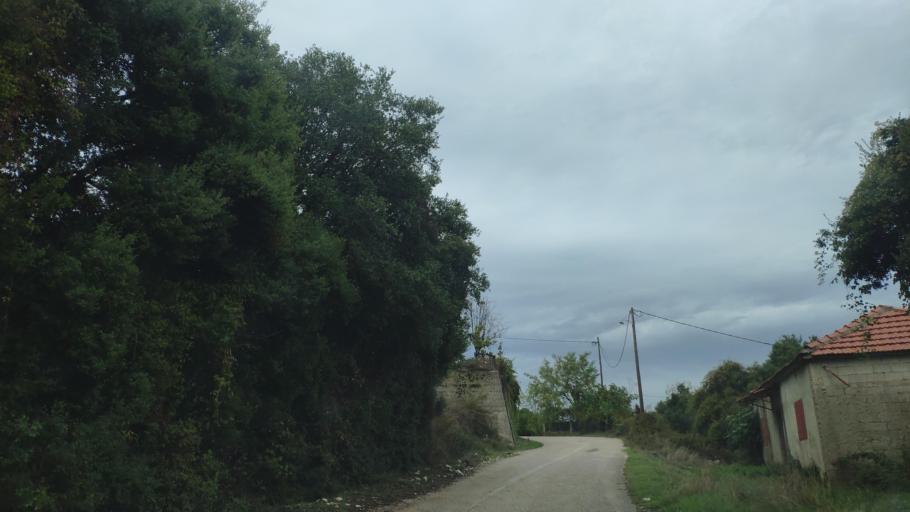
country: GR
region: Epirus
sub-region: Nomos Thesprotias
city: Paramythia
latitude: 39.4615
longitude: 20.6756
